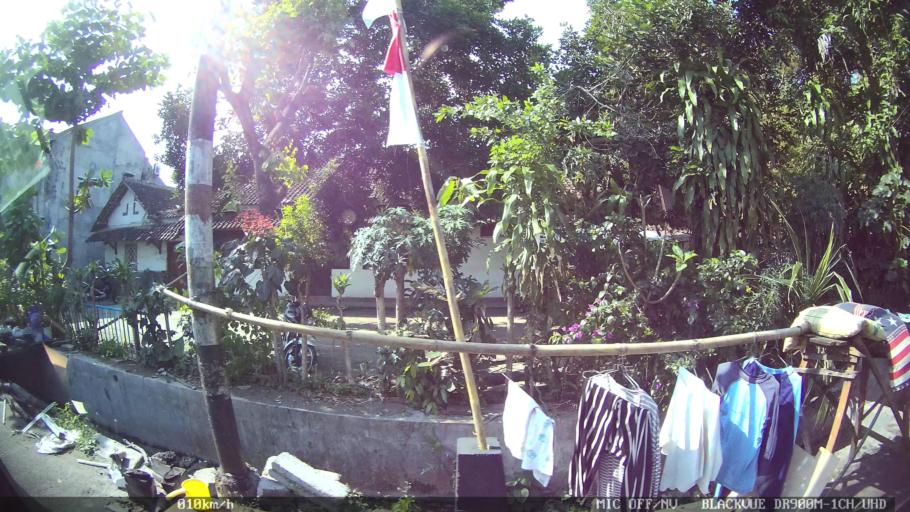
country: ID
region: Daerah Istimewa Yogyakarta
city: Sewon
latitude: -7.8310
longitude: 110.3921
